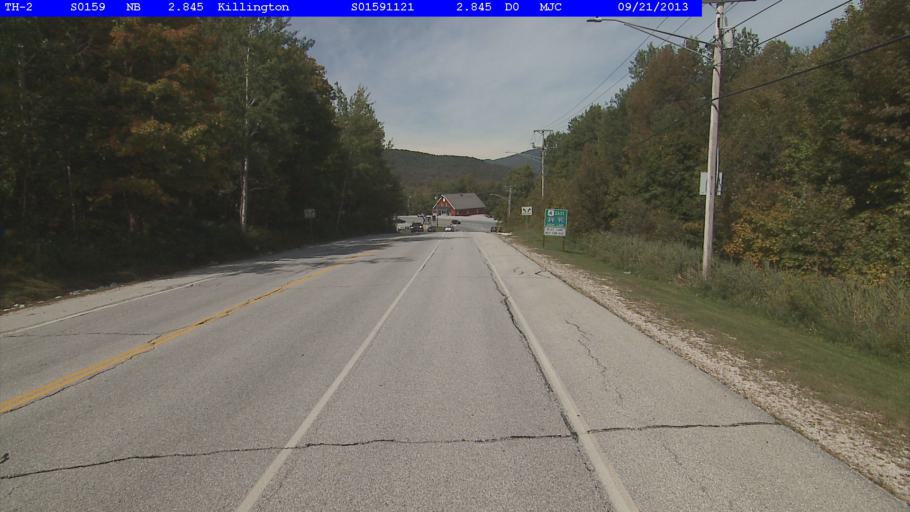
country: US
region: Vermont
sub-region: Rutland County
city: Rutland
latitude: 43.6665
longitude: -72.8024
